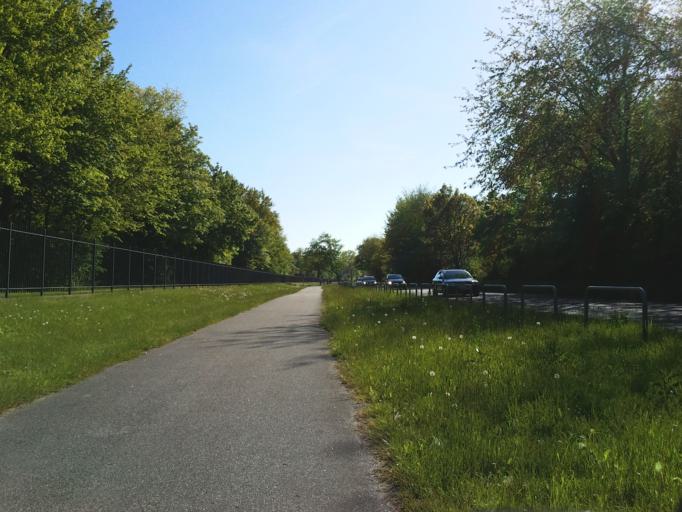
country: DE
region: Mecklenburg-Vorpommern
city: Warnemuende
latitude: 54.1829
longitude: 12.1255
